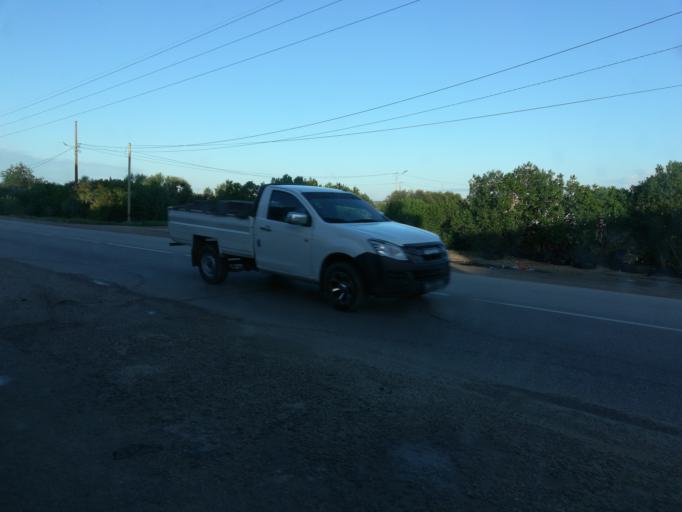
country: TN
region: Susah
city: Sidi Bou Ali
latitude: 36.0358
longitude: 10.3218
